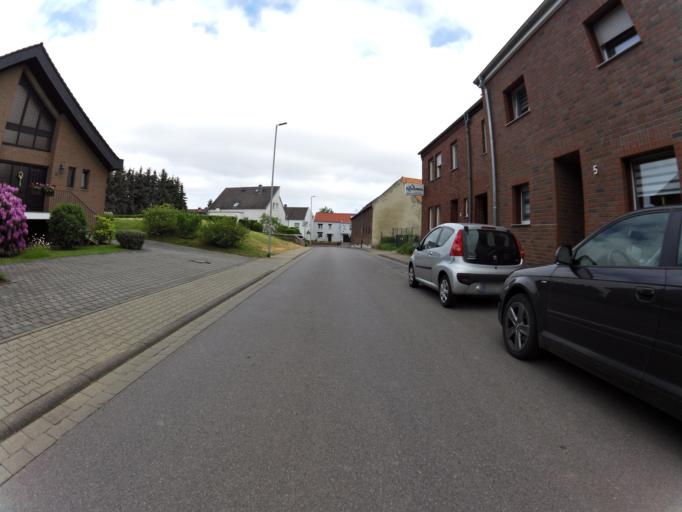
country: DE
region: North Rhine-Westphalia
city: Siersdorf
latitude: 50.9274
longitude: 6.2529
